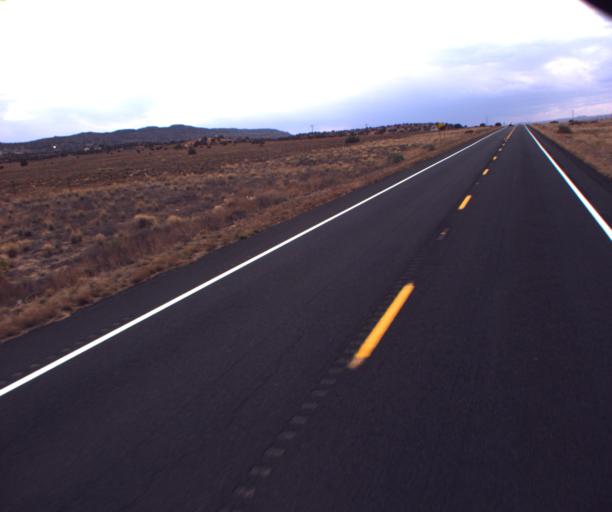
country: US
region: Arizona
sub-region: Coconino County
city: Kaibito
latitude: 36.4258
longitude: -110.7871
